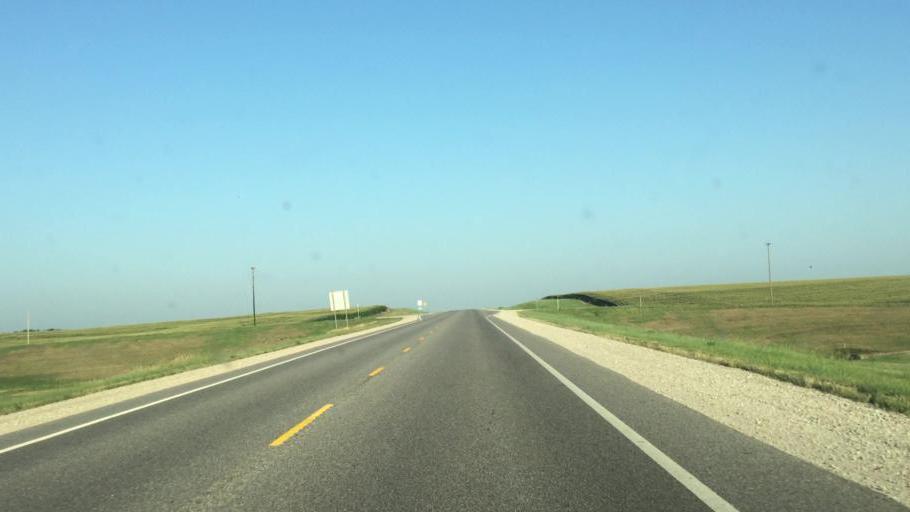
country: US
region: Kansas
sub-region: Doniphan County
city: Highland
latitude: 39.8421
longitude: -95.2818
